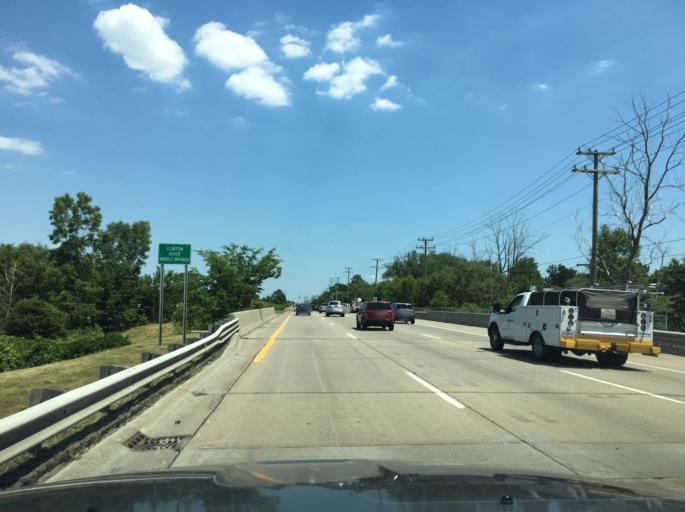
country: US
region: Michigan
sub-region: Macomb County
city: Clinton
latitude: 42.6282
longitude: -82.9319
